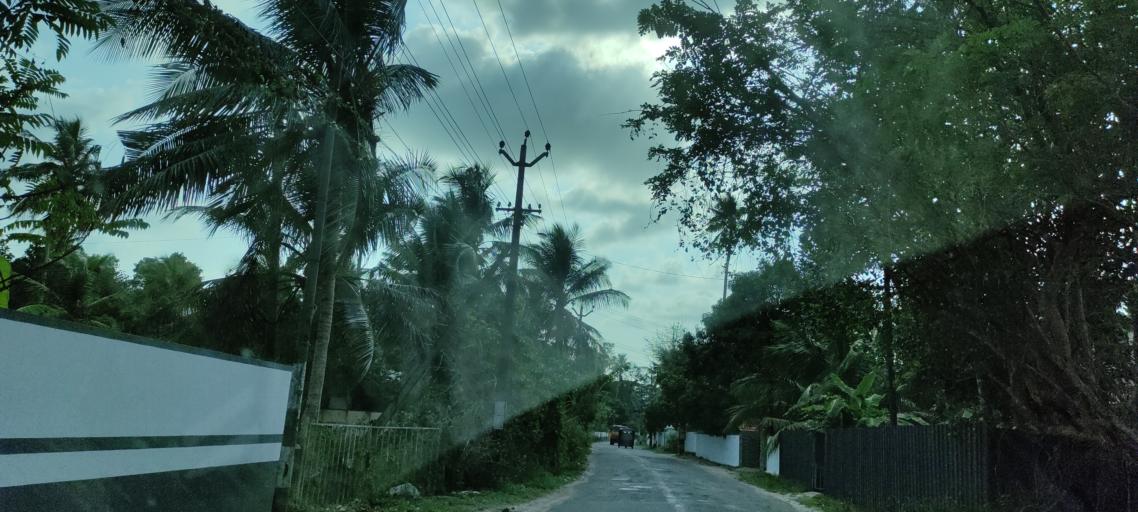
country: IN
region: Kerala
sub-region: Alappuzha
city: Vayalar
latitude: 9.6877
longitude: 76.3205
